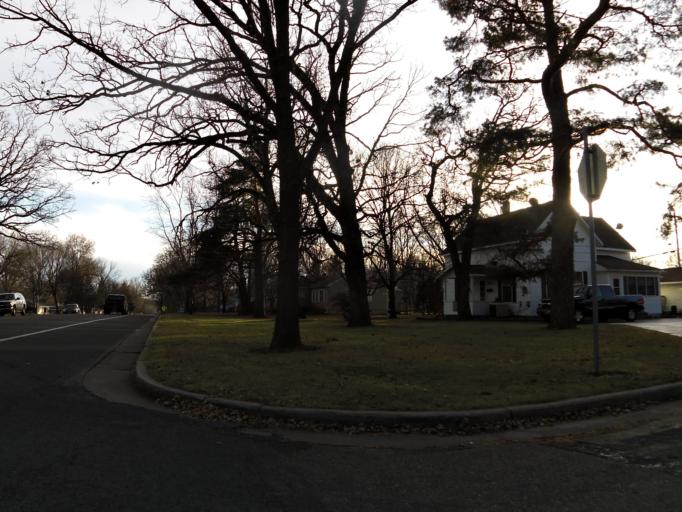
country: US
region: Wisconsin
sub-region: Pierce County
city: River Falls
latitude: 44.8617
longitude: -92.6351
